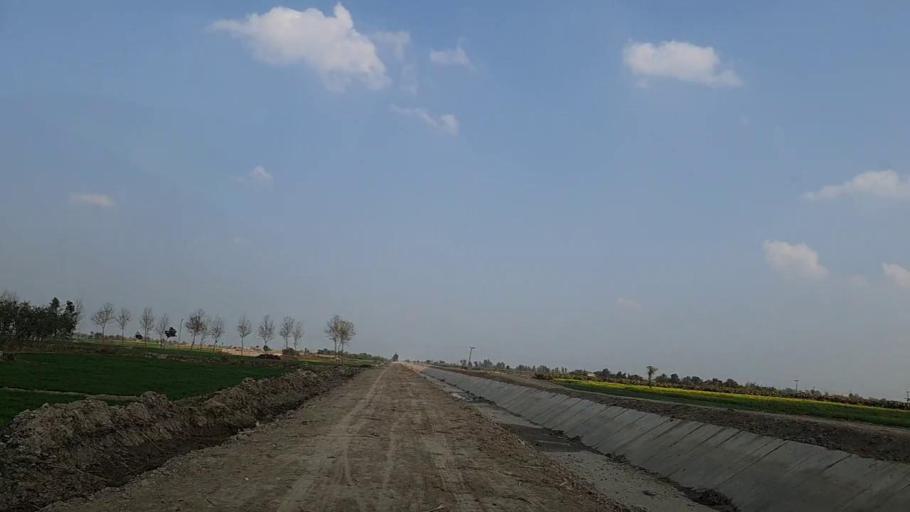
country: PK
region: Sindh
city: Sakrand
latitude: 26.1477
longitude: 68.3681
